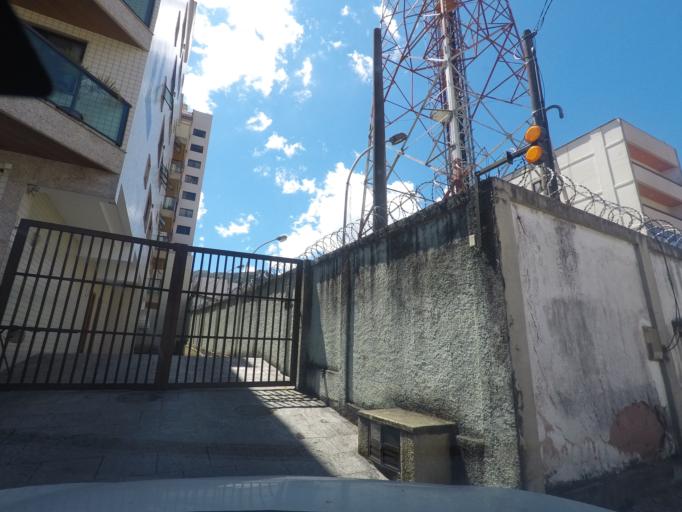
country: BR
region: Rio de Janeiro
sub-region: Teresopolis
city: Teresopolis
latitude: -22.4364
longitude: -42.9777
